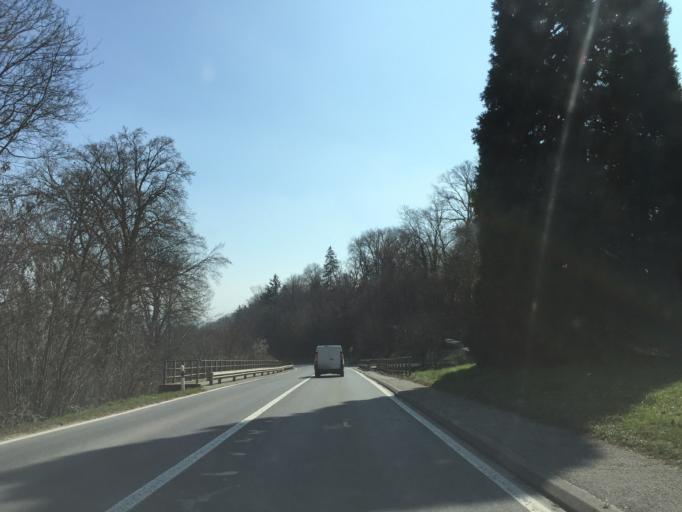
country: CH
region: Vaud
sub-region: Morges District
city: Cossonay
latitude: 46.6109
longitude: 6.5131
